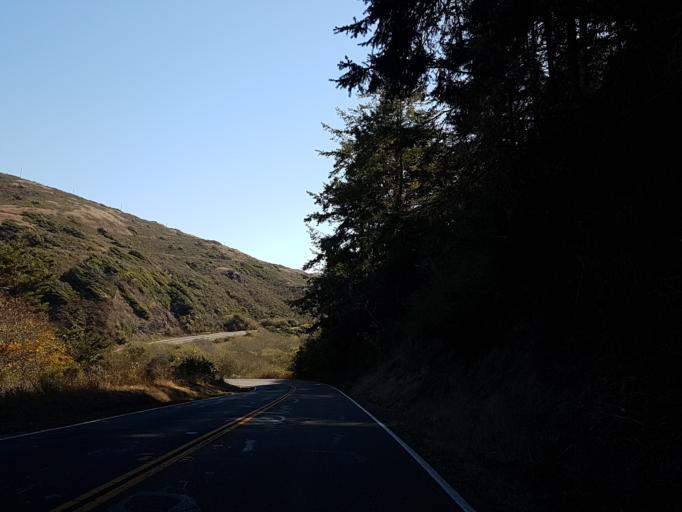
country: US
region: California
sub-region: Sonoma County
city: Monte Rio
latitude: 38.4724
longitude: -123.1552
